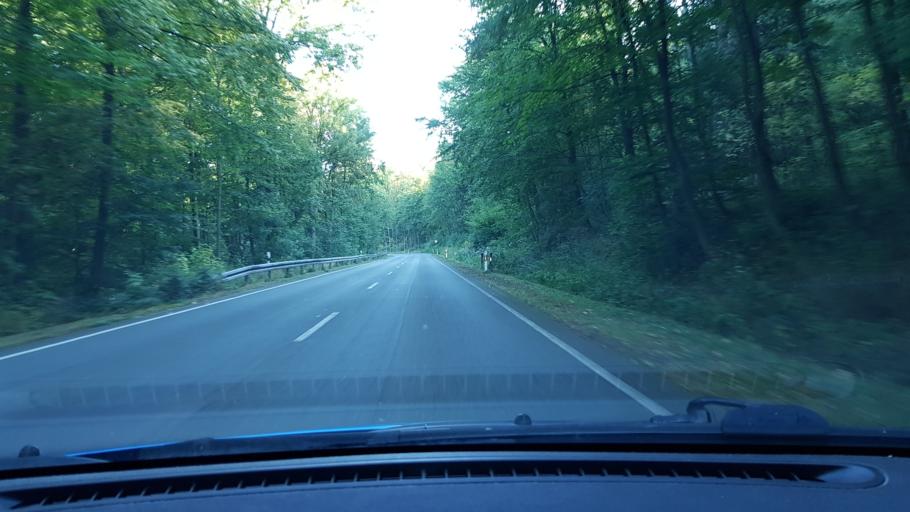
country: DE
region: Lower Saxony
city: Barsinghausen
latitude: 52.2619
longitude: 9.4671
